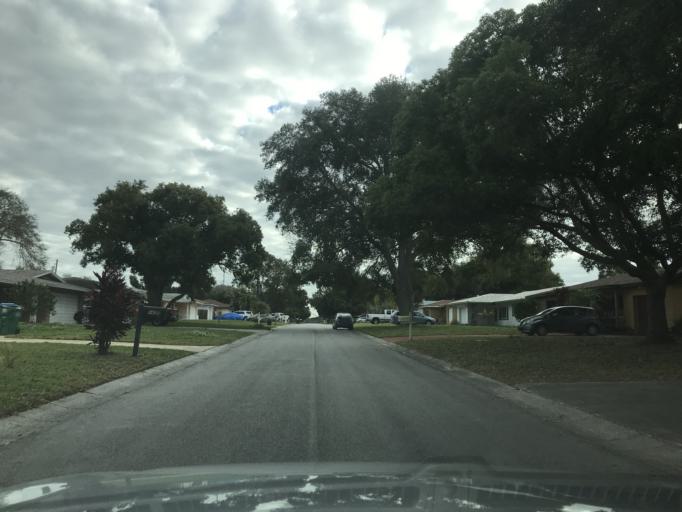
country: US
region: Florida
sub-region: Pinellas County
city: Belleair
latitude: 27.9453
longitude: -82.7782
